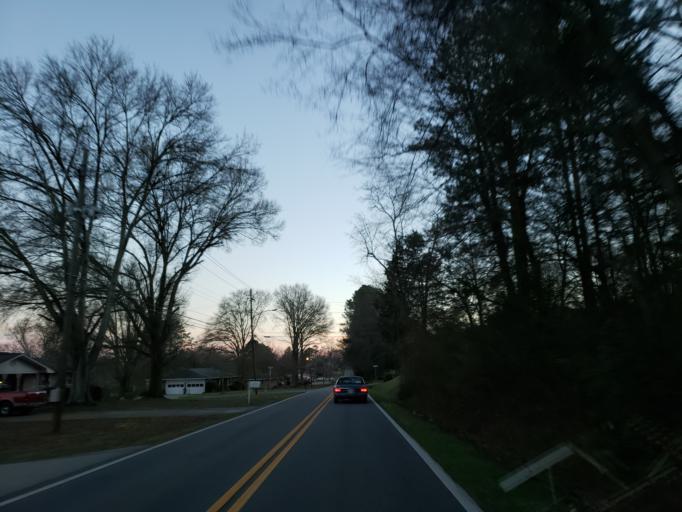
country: US
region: Georgia
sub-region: Bartow County
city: Cartersville
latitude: 34.2015
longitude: -84.8195
